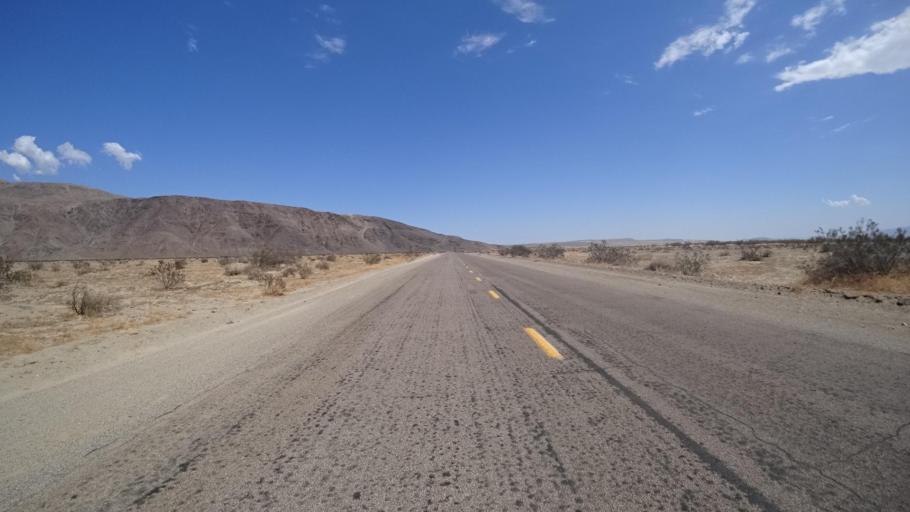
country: US
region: California
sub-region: San Diego County
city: Borrego Springs
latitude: 33.3008
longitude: -116.3336
